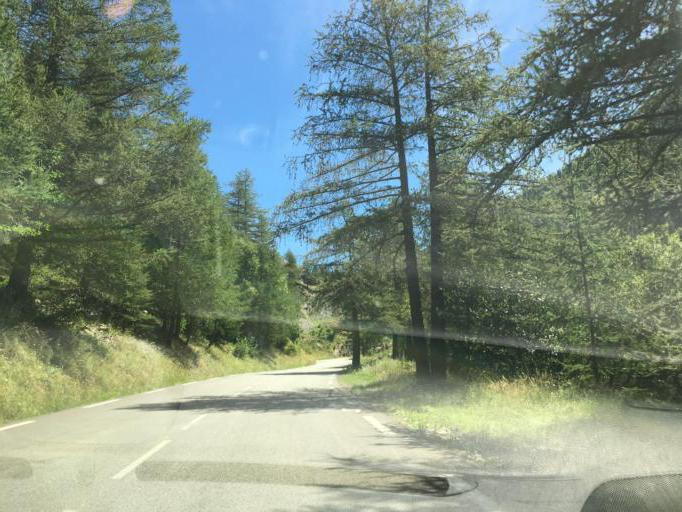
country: IT
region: Piedmont
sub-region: Provincia di Cuneo
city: Vinadio
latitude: 44.2094
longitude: 7.1063
